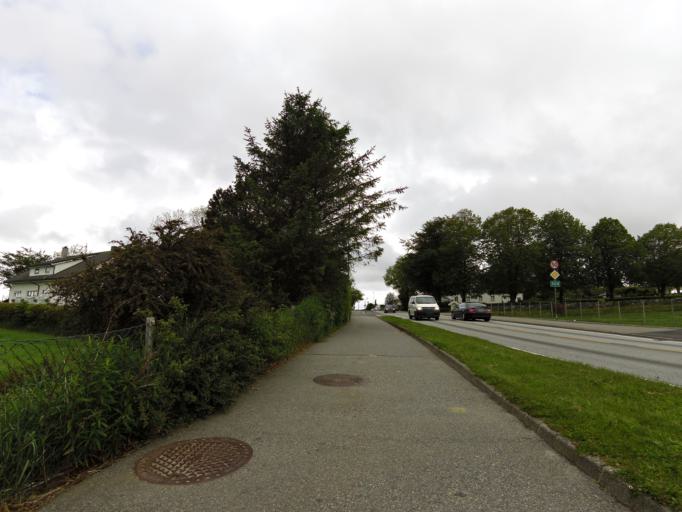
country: NO
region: Rogaland
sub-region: Randaberg
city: Randaberg
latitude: 58.9514
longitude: 5.6449
